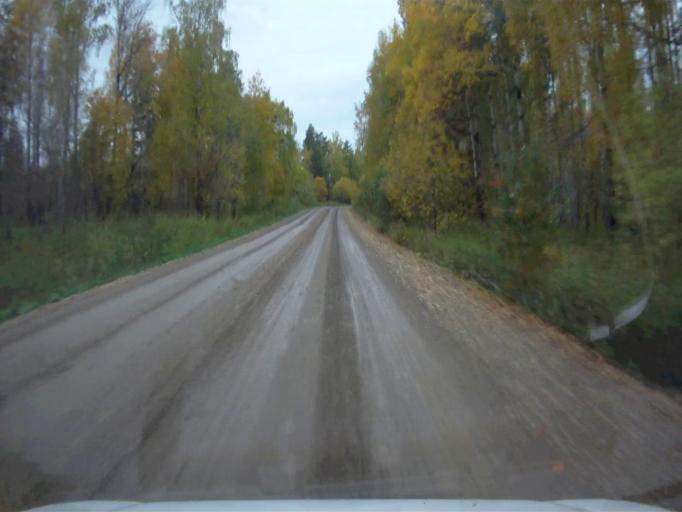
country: RU
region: Chelyabinsk
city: Nyazepetrovsk
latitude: 56.1105
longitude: 59.3727
